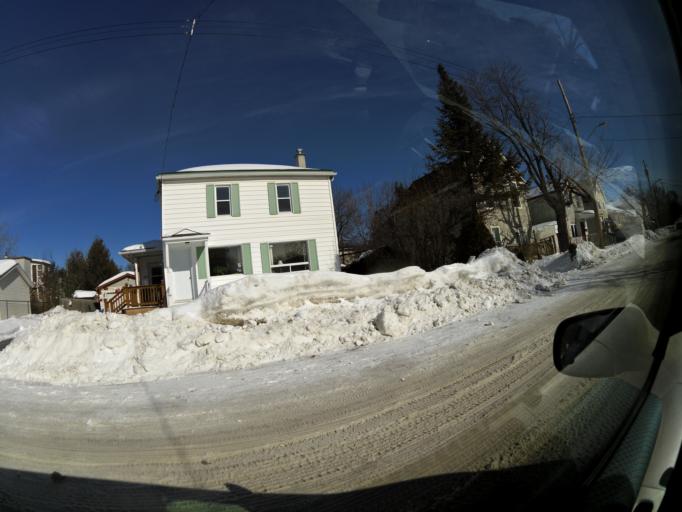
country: CA
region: Ontario
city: Ottawa
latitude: 45.4424
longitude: -75.6681
